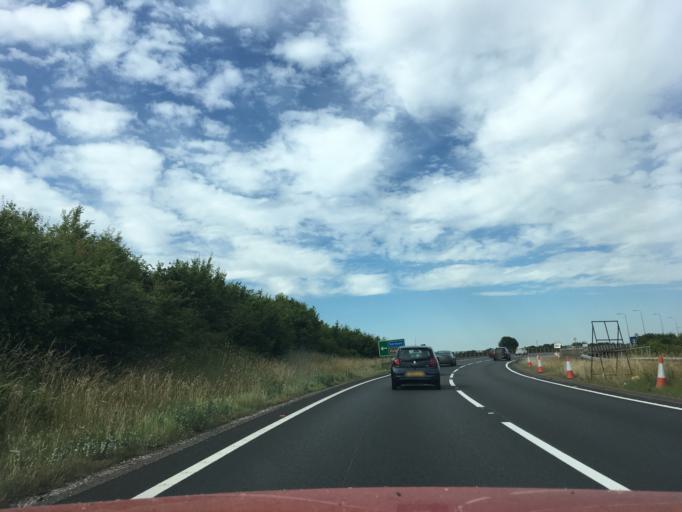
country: GB
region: England
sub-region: West Berkshire
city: Winterbourne
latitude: 51.4485
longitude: -1.3153
